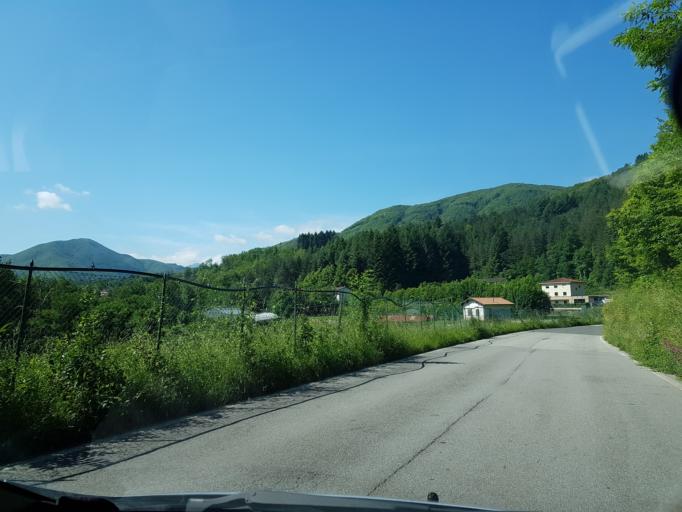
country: IT
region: Tuscany
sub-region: Provincia di Lucca
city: Camporgiano
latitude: 44.1671
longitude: 10.3290
